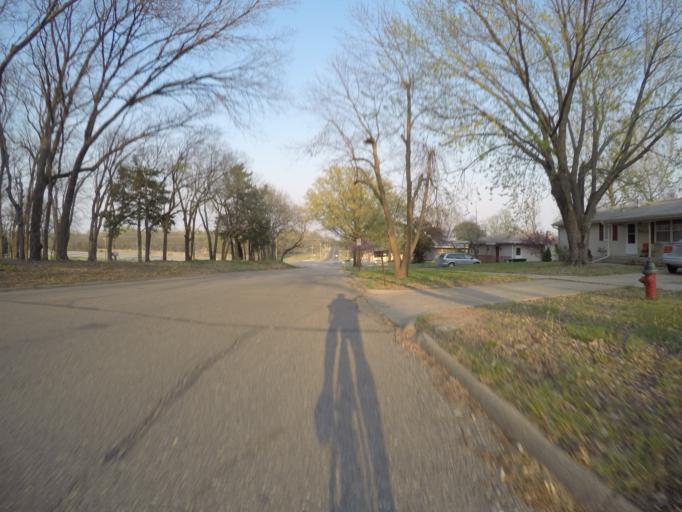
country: US
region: Kansas
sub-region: Riley County
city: Manhattan
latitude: 39.1964
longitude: -96.6140
